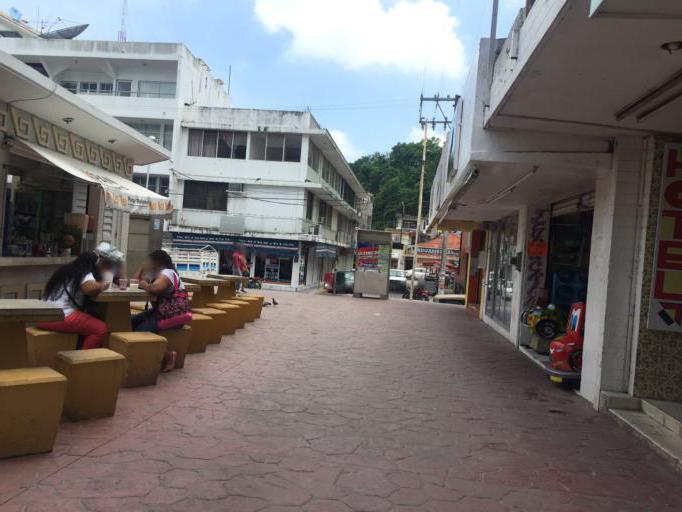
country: MX
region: Veracruz
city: Tuxpan de Rodriguez Cano
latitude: 20.9536
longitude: -97.4066
